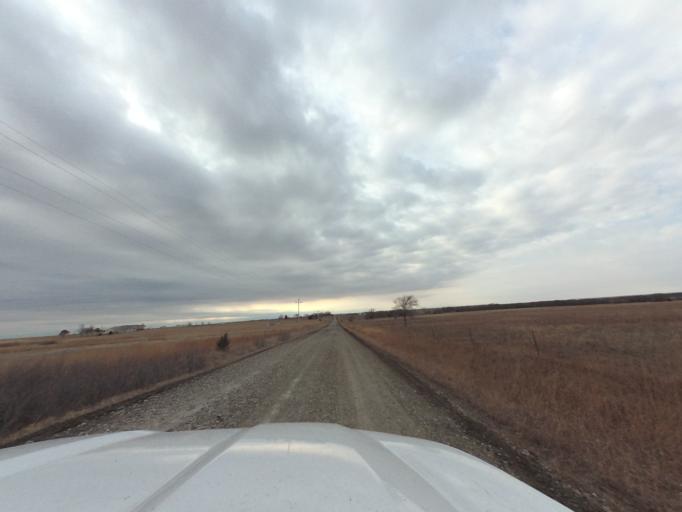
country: US
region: Kansas
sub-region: Chase County
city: Cottonwood Falls
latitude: 38.4467
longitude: -96.3731
